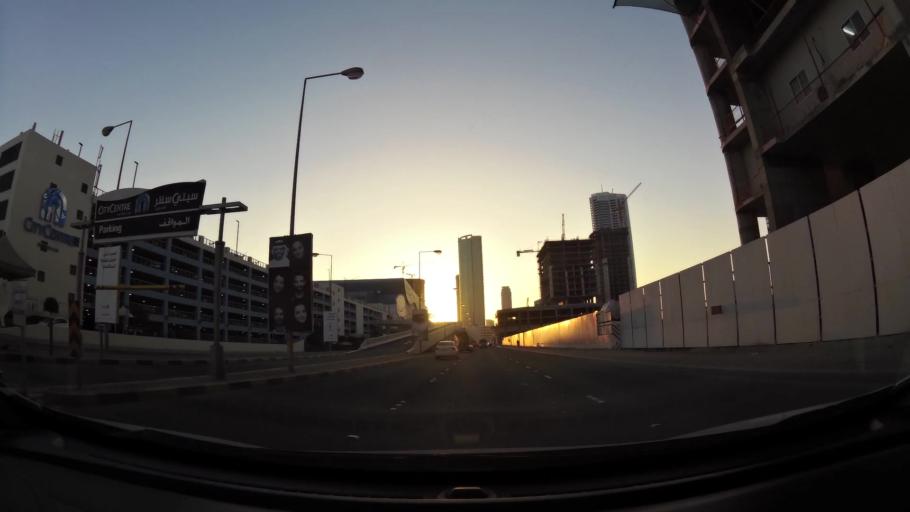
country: BH
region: Manama
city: Jidd Hafs
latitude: 26.2351
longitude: 50.5556
